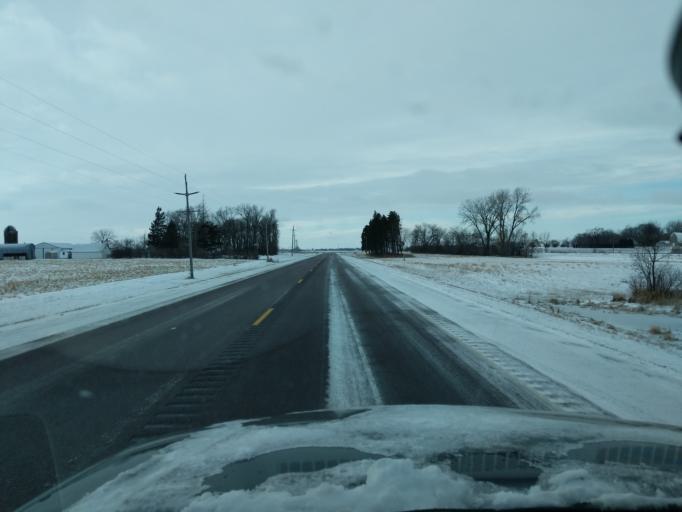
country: US
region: Minnesota
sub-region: McLeod County
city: Hutchinson
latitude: 44.7248
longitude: -94.4198
